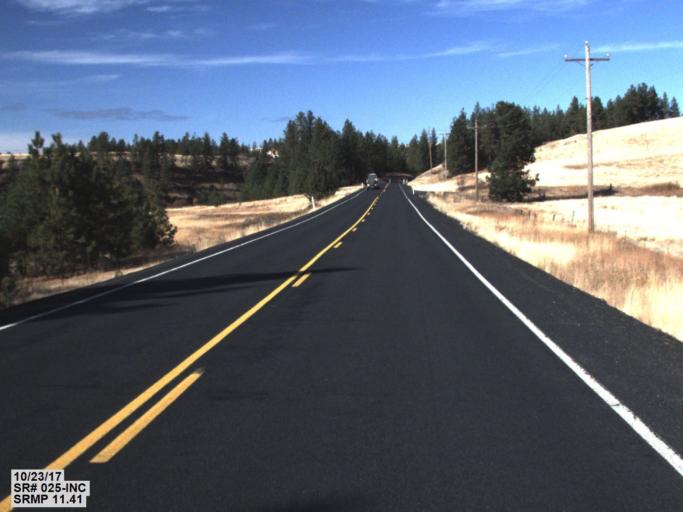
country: US
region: Washington
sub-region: Lincoln County
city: Davenport
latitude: 47.8127
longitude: -118.1805
